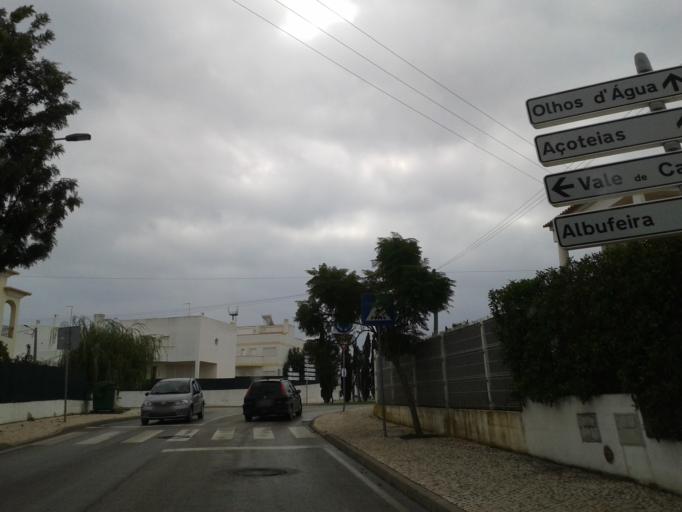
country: PT
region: Faro
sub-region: Loule
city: Boliqueime
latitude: 37.1019
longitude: -8.1845
